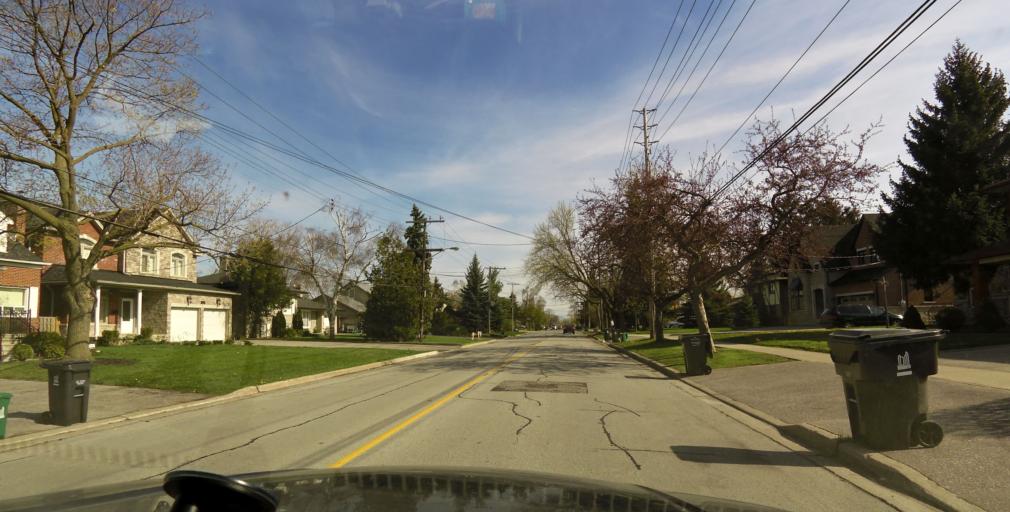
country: CA
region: Ontario
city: Etobicoke
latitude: 43.6332
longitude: -79.5668
